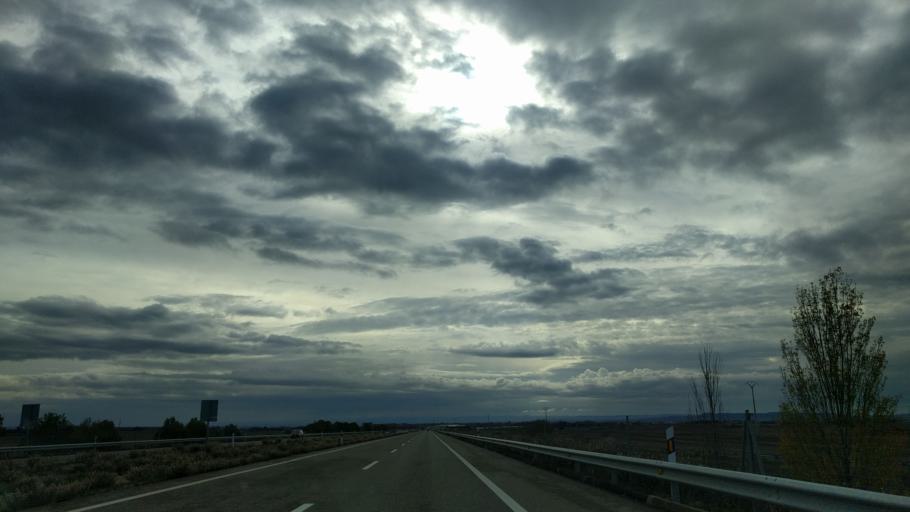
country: ES
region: Aragon
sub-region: Provincia de Huesca
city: Igries
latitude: 42.2028
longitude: -0.4359
